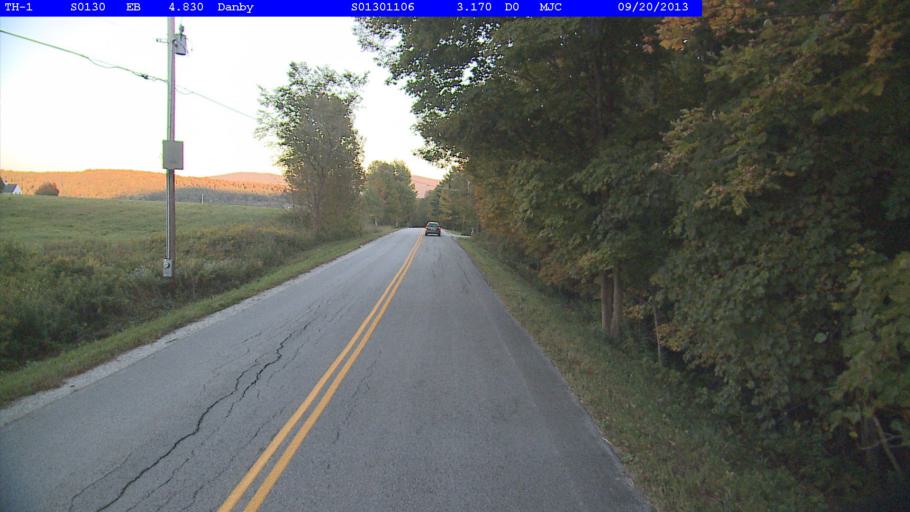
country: US
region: Vermont
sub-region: Bennington County
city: Manchester Center
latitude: 43.3584
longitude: -73.0675
